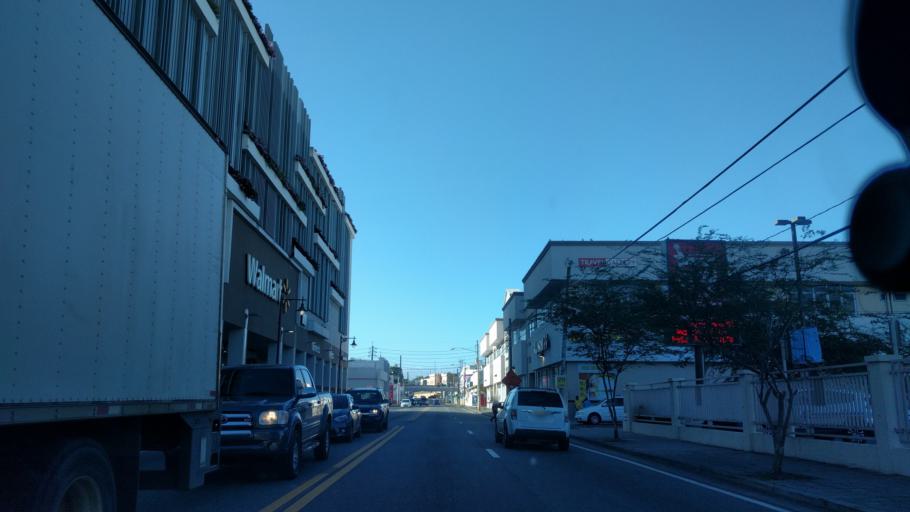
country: PR
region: San Juan
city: San Juan
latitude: 18.4484
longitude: -66.0759
